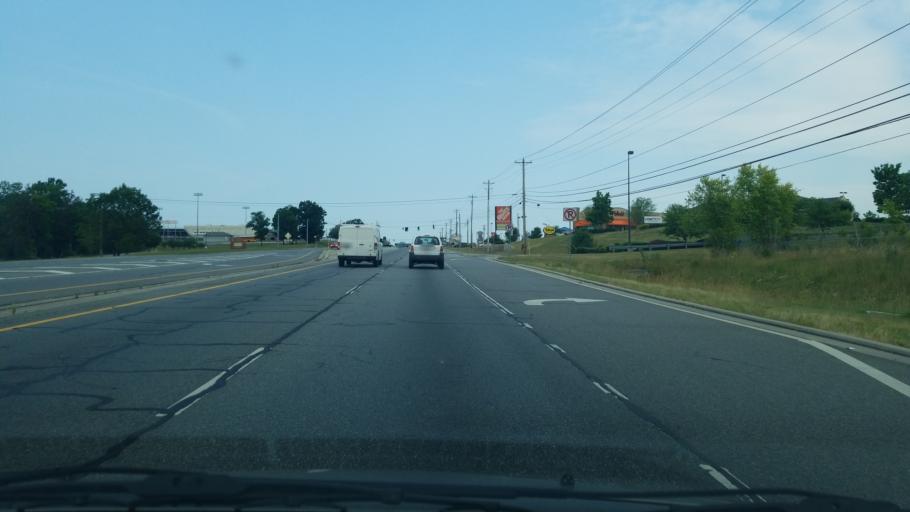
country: US
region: Georgia
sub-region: Catoosa County
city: Fort Oglethorpe
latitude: 34.9456
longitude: -85.2289
